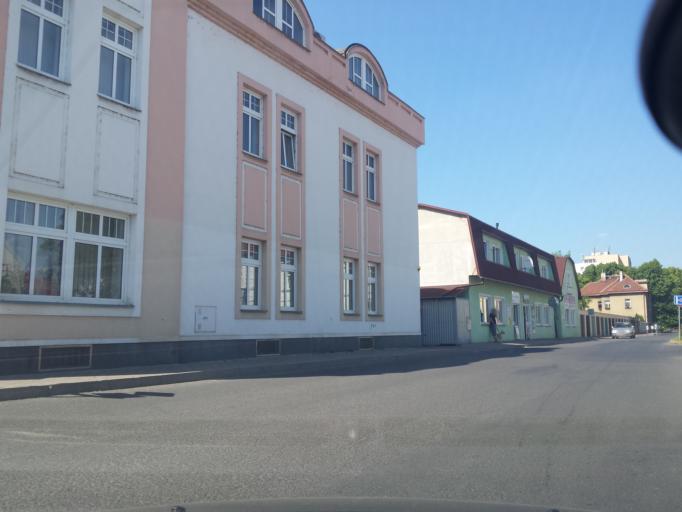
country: CZ
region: Central Bohemia
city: Kralupy nad Vltavou
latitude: 50.2410
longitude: 14.3083
